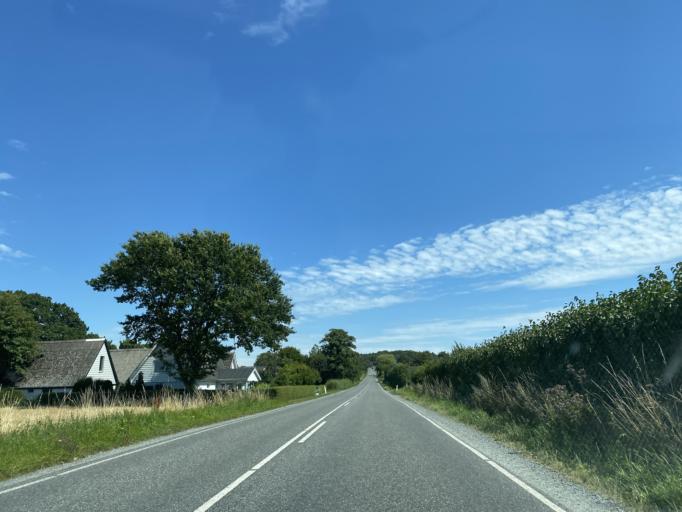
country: DK
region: South Denmark
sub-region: Faaborg-Midtfyn Kommune
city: Ringe
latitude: 55.2082
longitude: 10.3848
